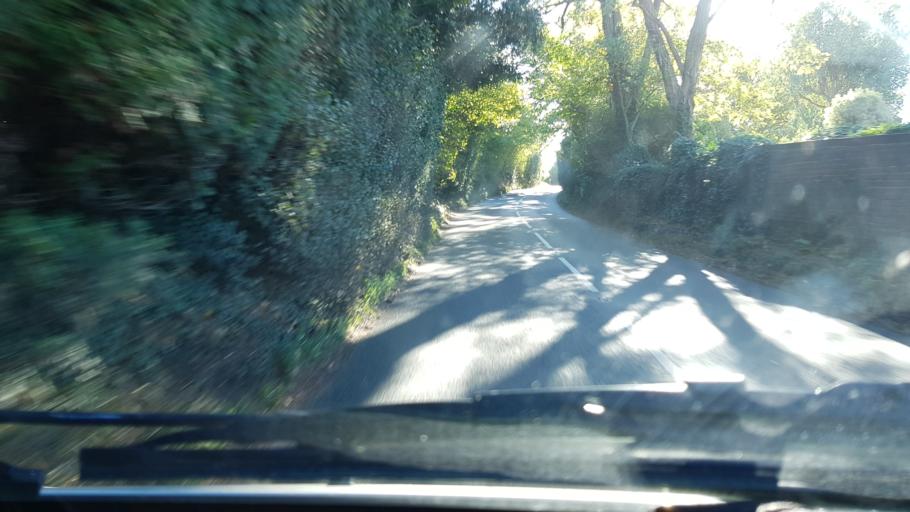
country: GB
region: England
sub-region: Surrey
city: Chilworth
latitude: 51.1940
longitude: -0.5333
